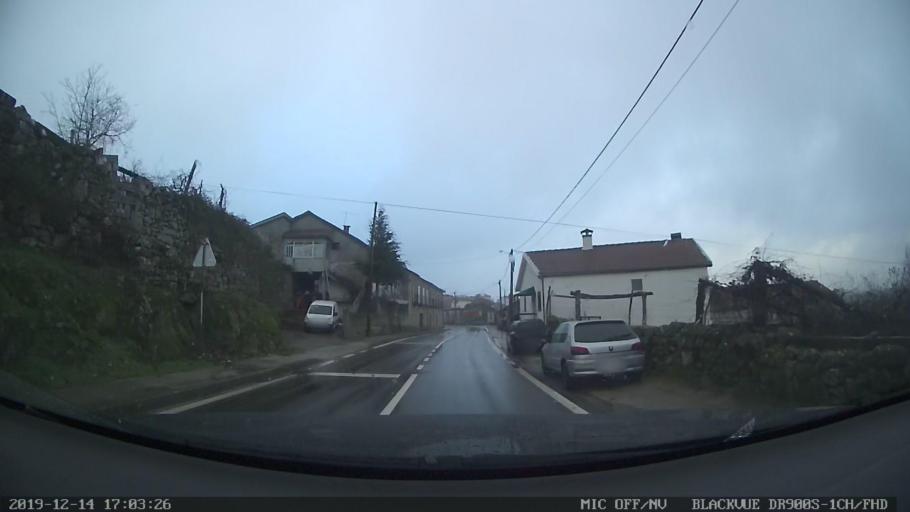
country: PT
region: Vila Real
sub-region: Vila Pouca de Aguiar
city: Vila Pouca de Aguiar
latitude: 41.4427
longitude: -7.5711
